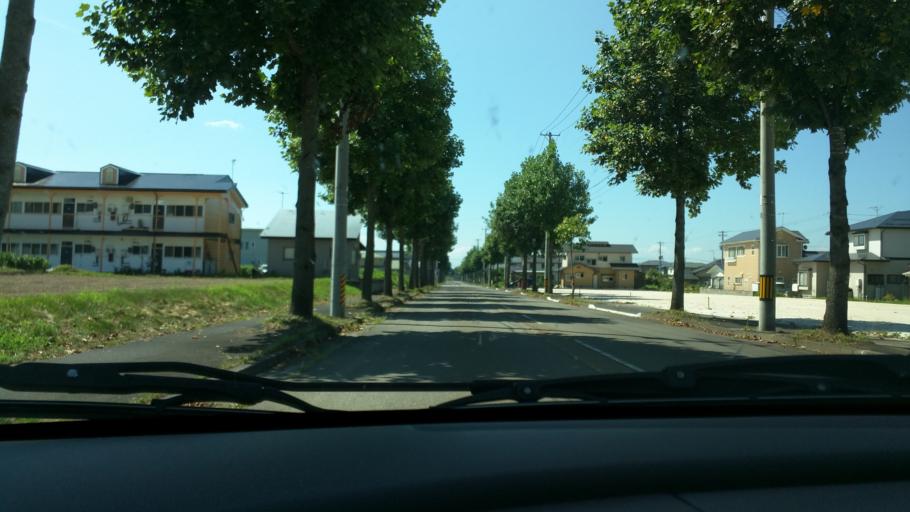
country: JP
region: Fukushima
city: Kitakata
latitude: 37.6693
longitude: 139.8684
